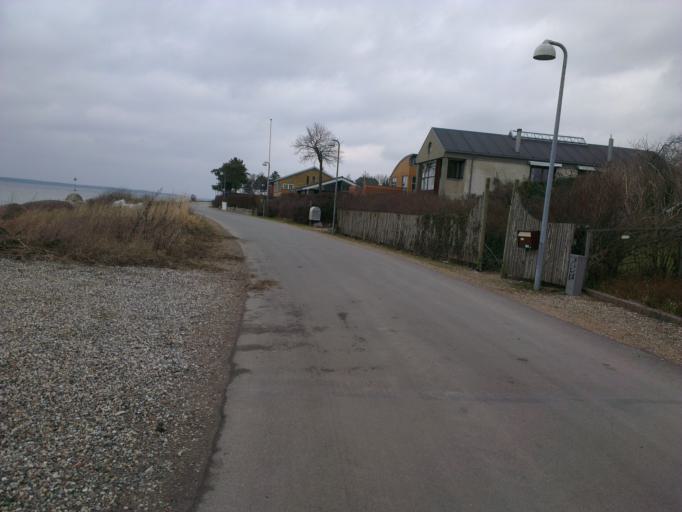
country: DK
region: Capital Region
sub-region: Frederikssund Kommune
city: Frederikssund
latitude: 55.8477
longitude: 12.0447
